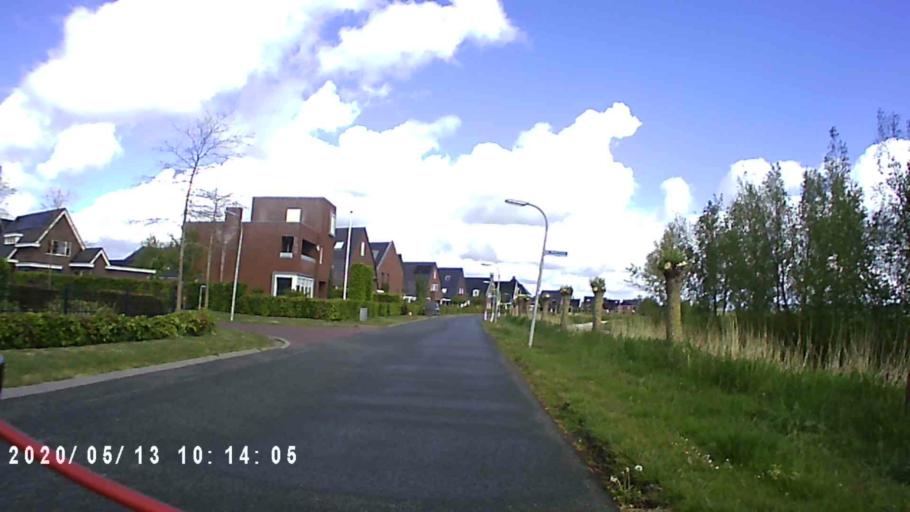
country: NL
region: Groningen
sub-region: Gemeente Zuidhorn
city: Zuidhorn
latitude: 53.2458
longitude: 6.4176
